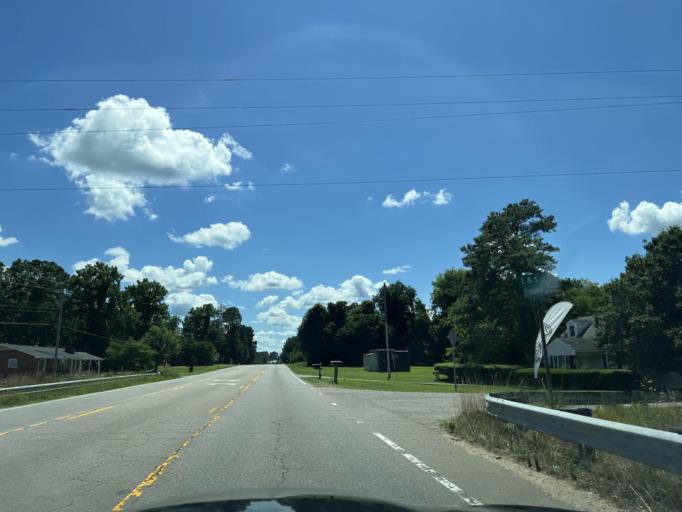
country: US
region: North Carolina
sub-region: Lee County
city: Sanford
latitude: 35.4432
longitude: -79.1773
